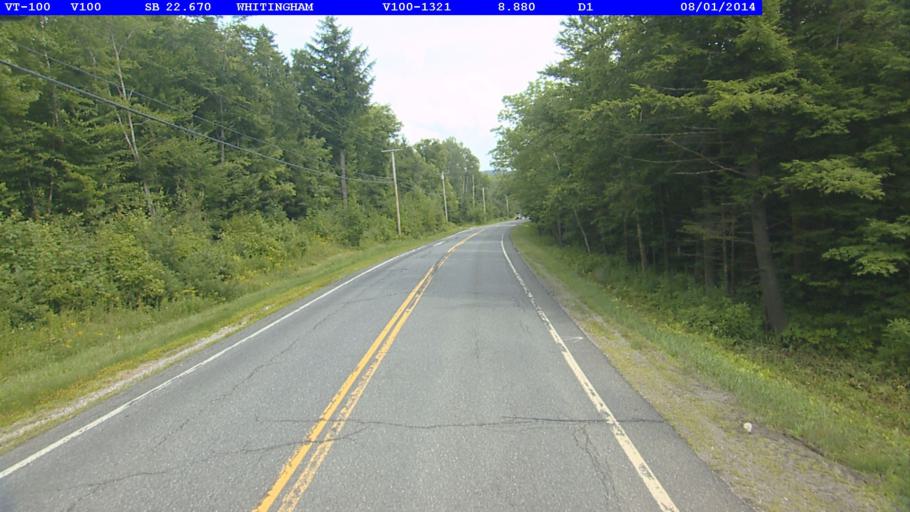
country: US
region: Vermont
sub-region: Windham County
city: Dover
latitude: 42.8085
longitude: -72.8379
